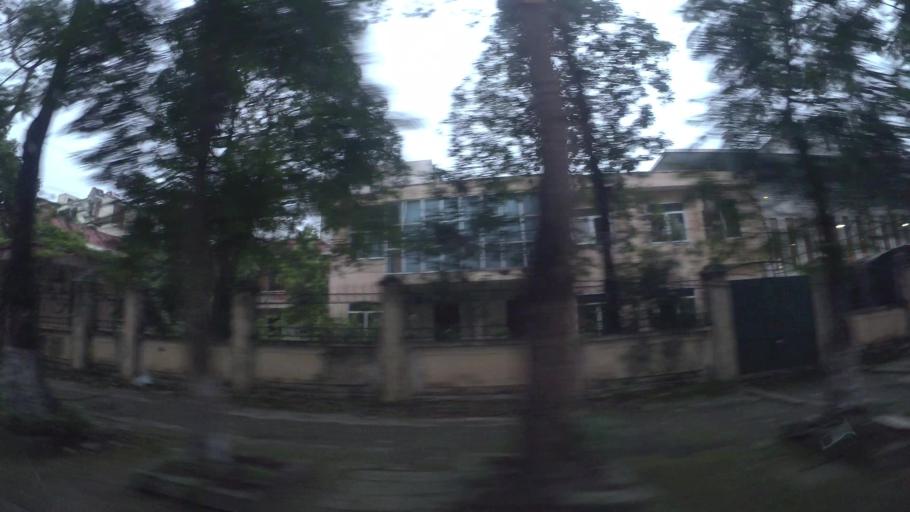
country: VN
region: Ha Noi
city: Hai BaTrung
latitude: 20.9873
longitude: 105.8321
